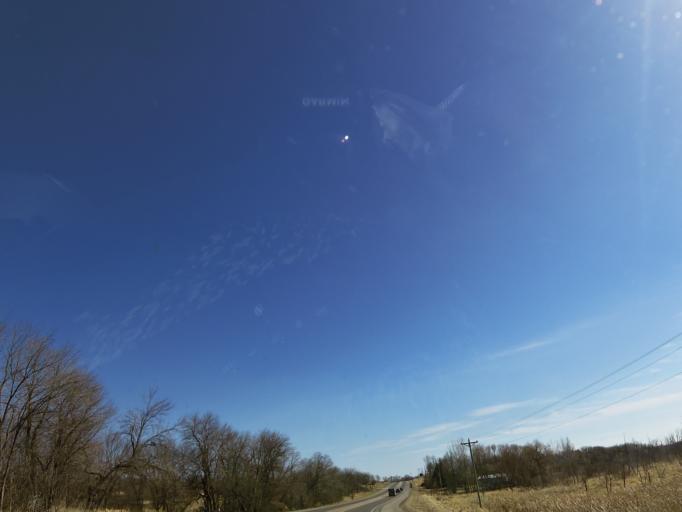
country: US
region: Minnesota
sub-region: Hennepin County
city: Greenfield
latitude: 45.0784
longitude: -93.7028
